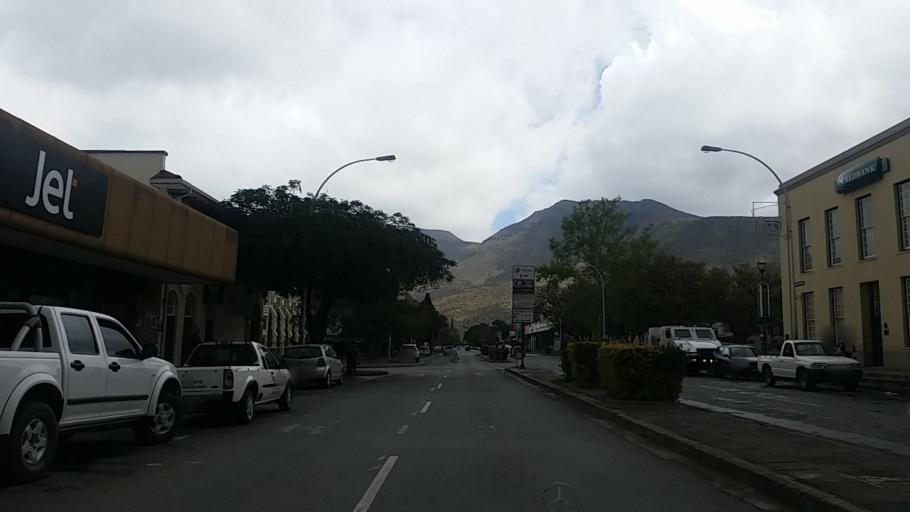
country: ZA
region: Eastern Cape
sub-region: Cacadu District Municipality
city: Graaff-Reinet
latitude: -32.2489
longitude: 24.5357
